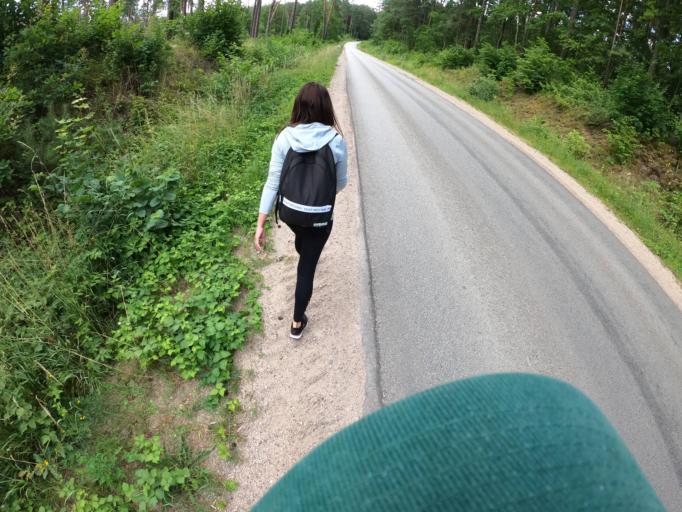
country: LT
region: Alytaus apskritis
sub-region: Alytus
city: Alytus
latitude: 54.4220
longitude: 24.0743
